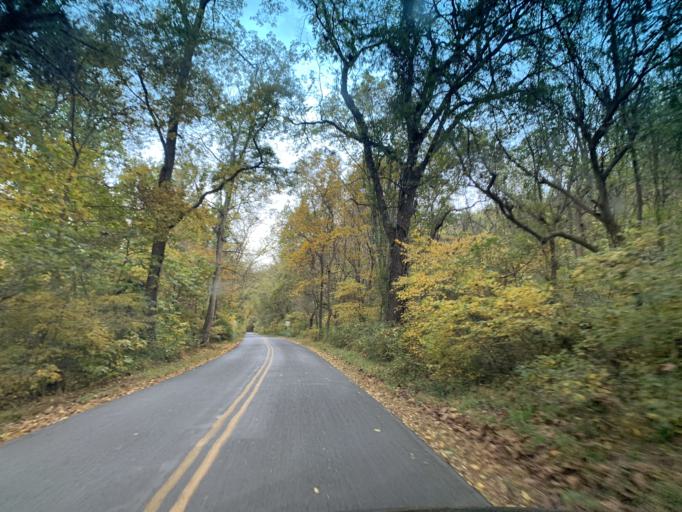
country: US
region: Maryland
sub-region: Harford County
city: Havre de Grace
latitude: 39.6171
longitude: -76.1539
